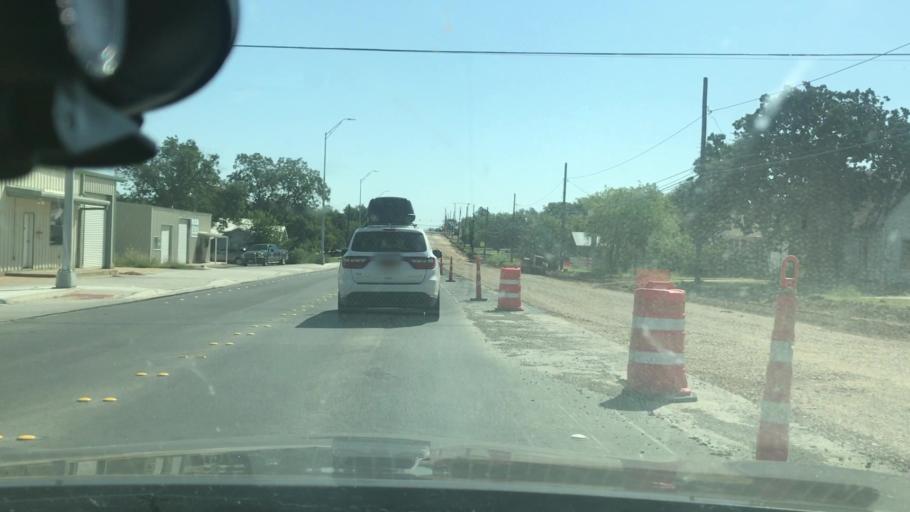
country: US
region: Texas
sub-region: Stephens County
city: Breckenridge
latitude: 32.7555
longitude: -98.8903
